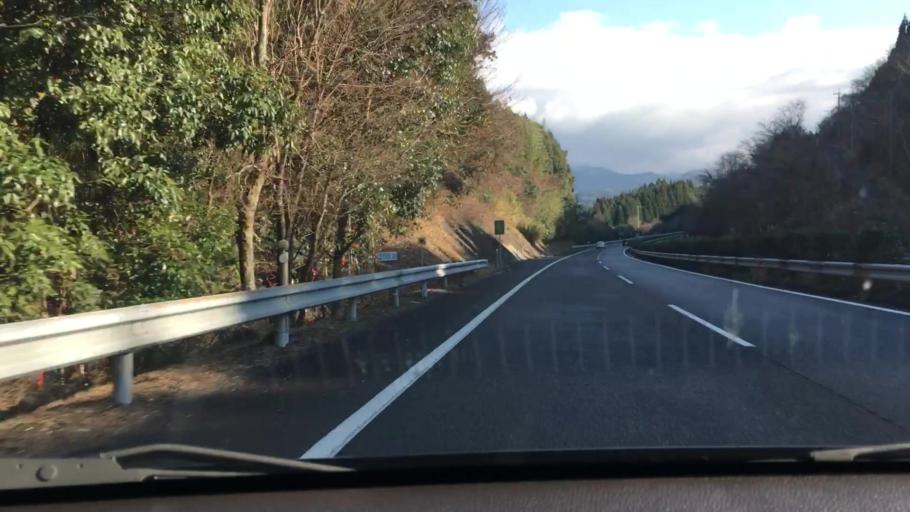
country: JP
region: Kumamoto
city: Hitoyoshi
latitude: 32.1799
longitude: 130.7852
